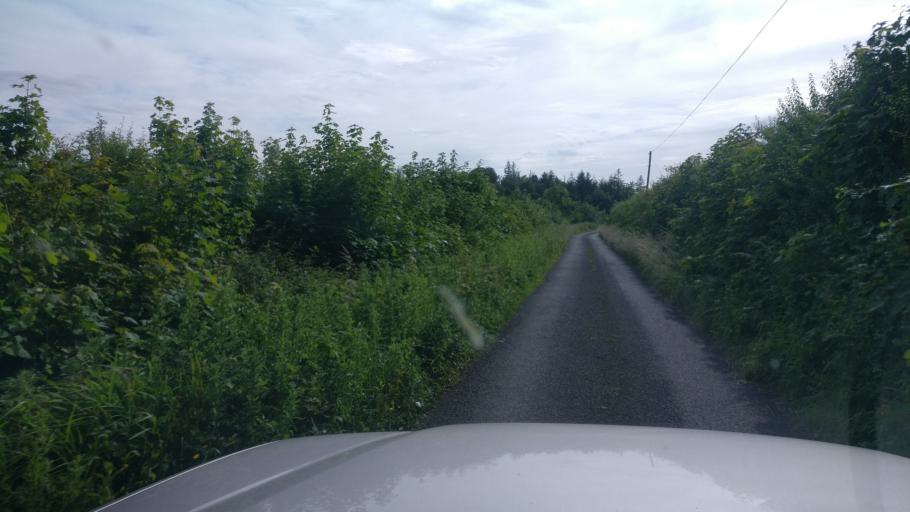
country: IE
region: Connaught
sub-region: County Galway
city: Gort
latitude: 53.1082
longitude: -8.7272
